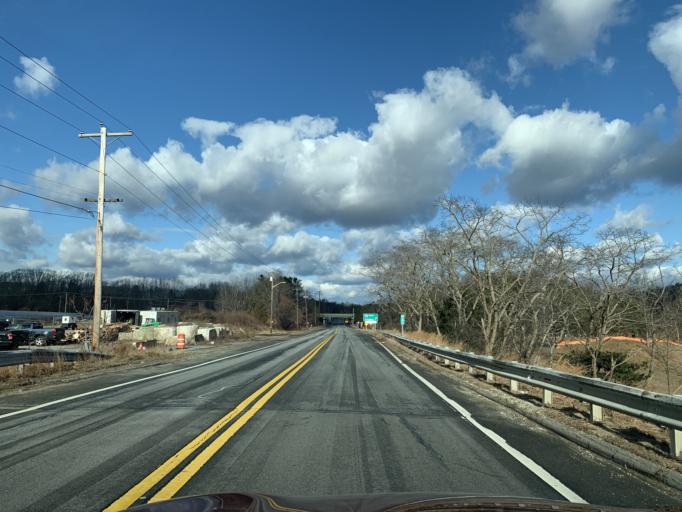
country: US
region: Massachusetts
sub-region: Essex County
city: Amesbury
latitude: 42.8365
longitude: -70.9356
